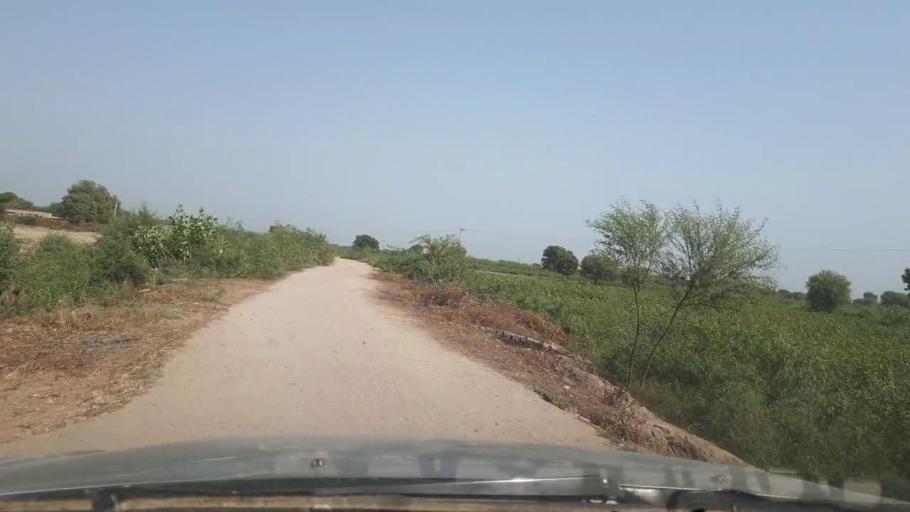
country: PK
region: Sindh
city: Tando Ghulam Ali
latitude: 25.1803
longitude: 68.8788
